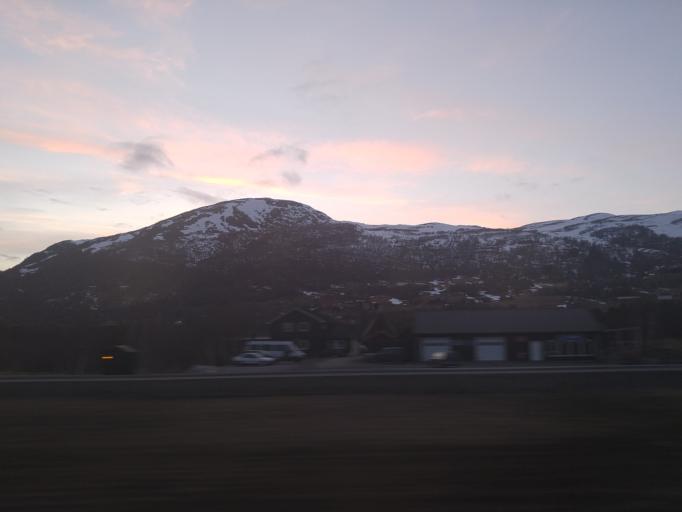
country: NO
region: Sor-Trondelag
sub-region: Oppdal
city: Oppdal
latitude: 62.6034
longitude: 9.7292
